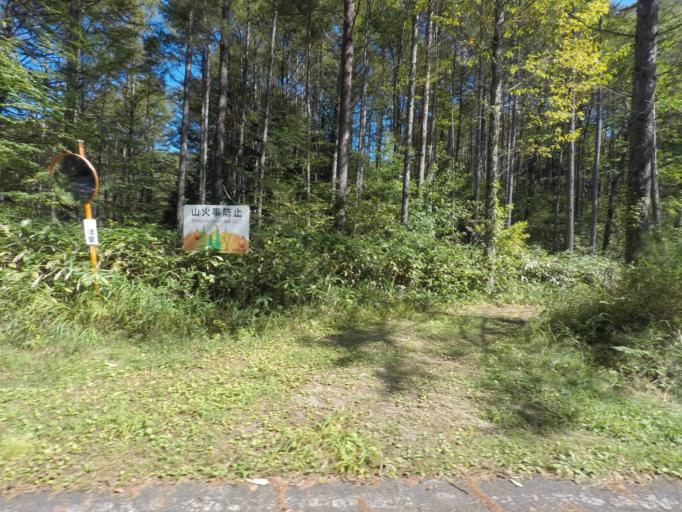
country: JP
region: Nagano
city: Shiojiri
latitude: 35.9987
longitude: 137.7341
